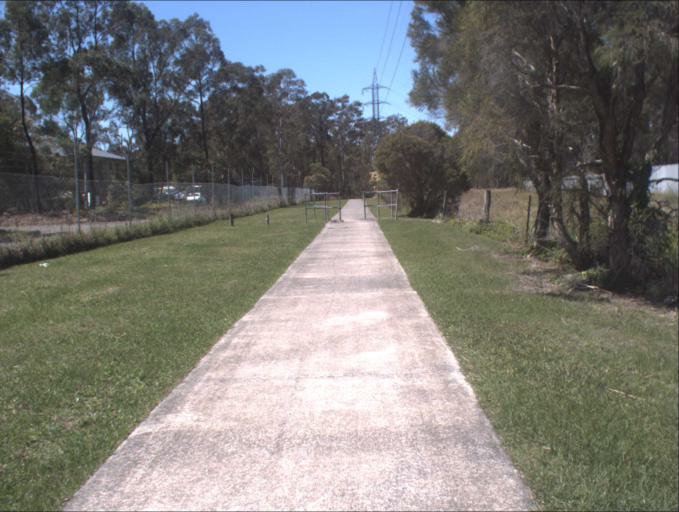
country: AU
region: Queensland
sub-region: Logan
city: Logan City
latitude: -27.6654
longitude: 153.0962
